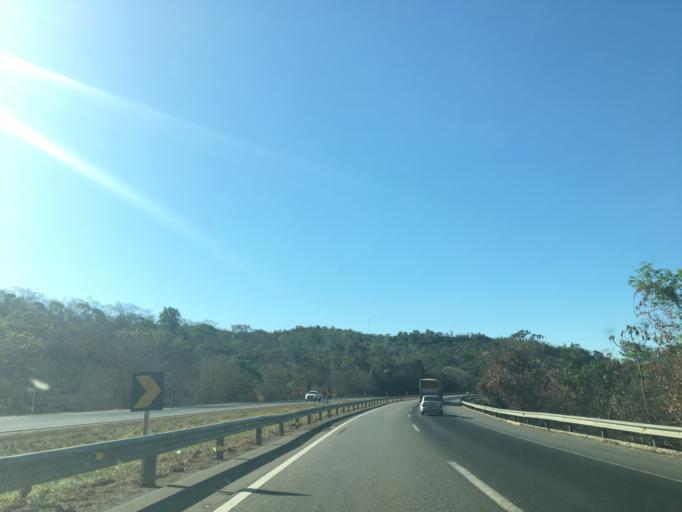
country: BR
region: Goias
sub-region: Hidrolandia
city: Hidrolandia
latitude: -17.0834
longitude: -49.2241
